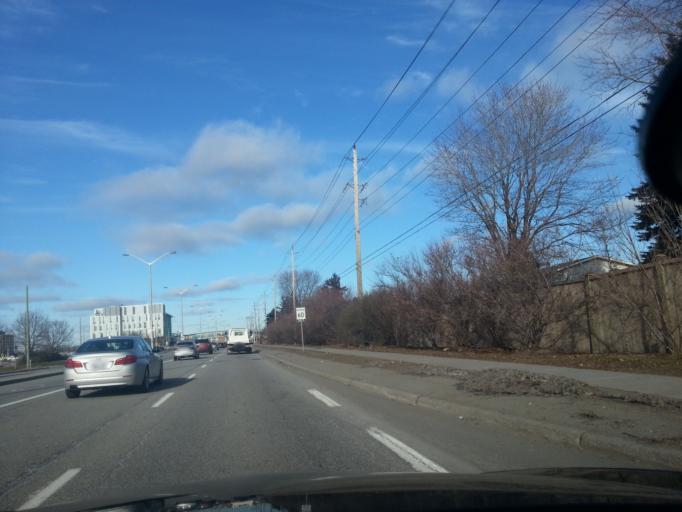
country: CA
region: Ontario
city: Bells Corners
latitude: 45.3442
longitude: -75.7578
